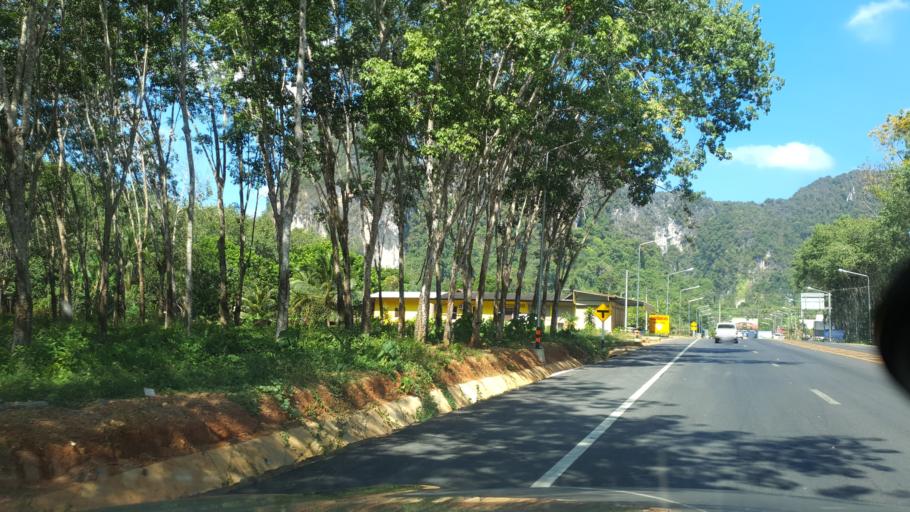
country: TH
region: Krabi
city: Krabi
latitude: 8.0769
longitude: 98.8574
